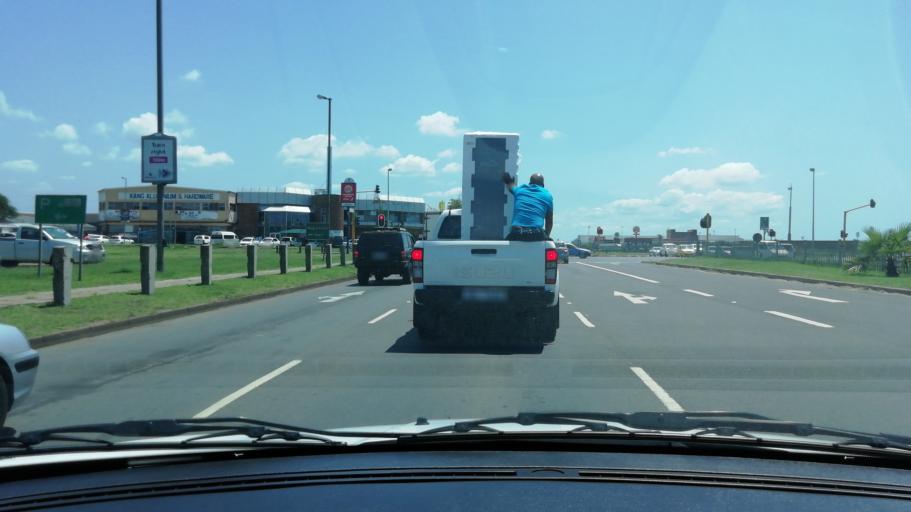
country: ZA
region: KwaZulu-Natal
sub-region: uThungulu District Municipality
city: Richards Bay
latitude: -28.7496
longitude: 32.0485
